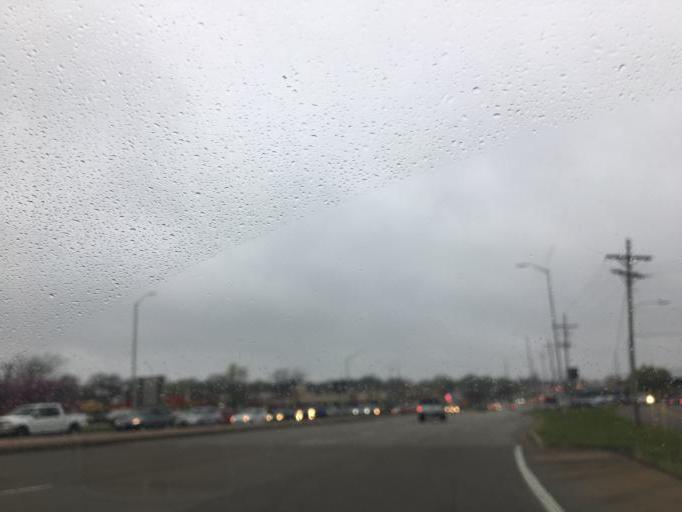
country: US
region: Kansas
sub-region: Johnson County
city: Olathe
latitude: 38.8862
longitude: -94.7917
